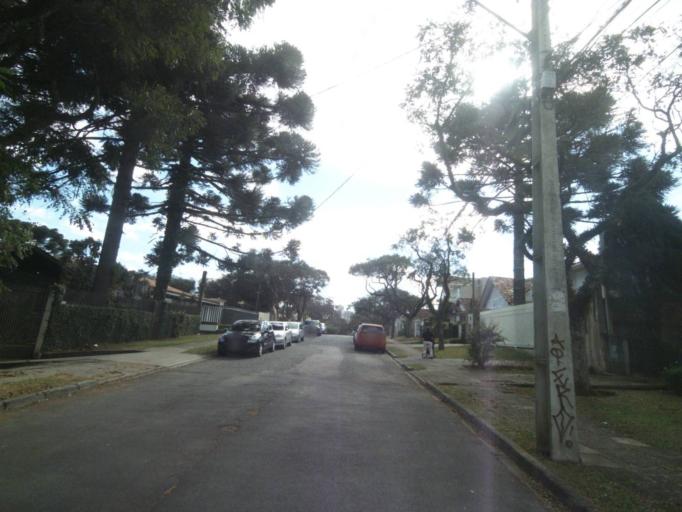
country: BR
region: Parana
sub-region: Curitiba
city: Curitiba
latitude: -25.4579
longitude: -49.2758
